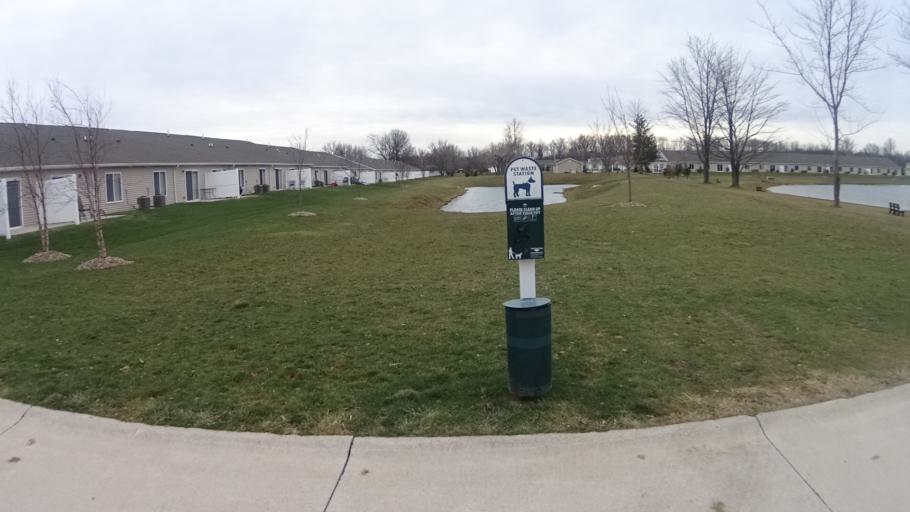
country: US
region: Ohio
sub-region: Lorain County
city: North Ridgeville
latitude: 41.3748
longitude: -81.9734
